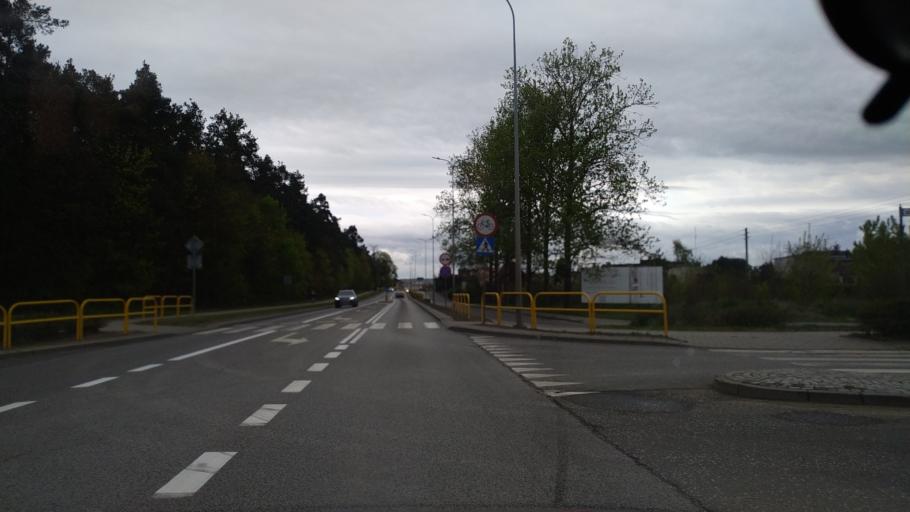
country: PL
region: Pomeranian Voivodeship
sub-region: Powiat starogardzki
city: Starogard Gdanski
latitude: 53.9566
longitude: 18.4900
